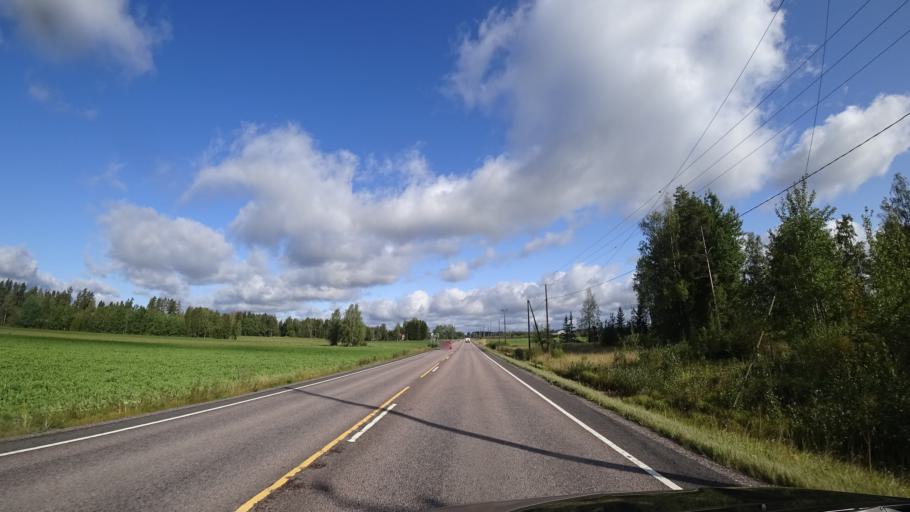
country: FI
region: Uusimaa
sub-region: Helsinki
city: Nurmijaervi
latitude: 60.5121
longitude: 24.9276
